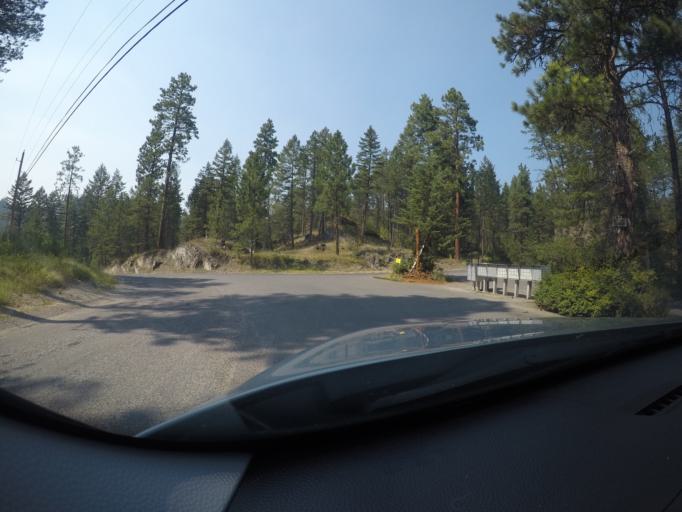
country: US
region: Montana
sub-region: Lake County
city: Polson
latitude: 47.7722
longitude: -114.1430
